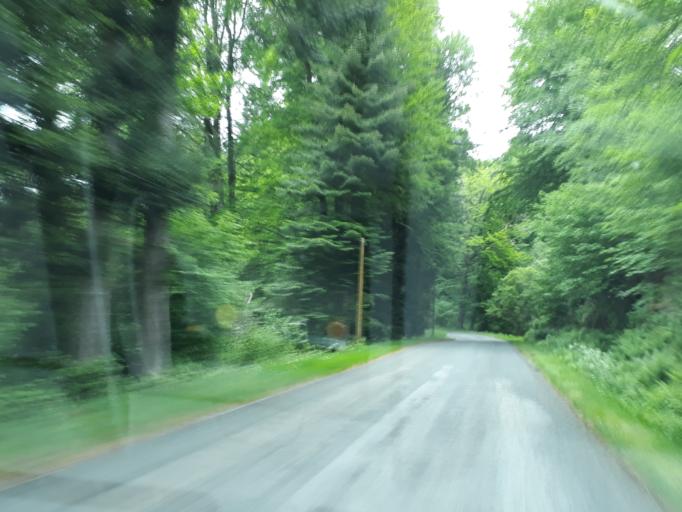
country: FR
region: Limousin
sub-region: Departement de la Haute-Vienne
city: Peyrat-le-Chateau
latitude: 45.8221
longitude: 1.8311
